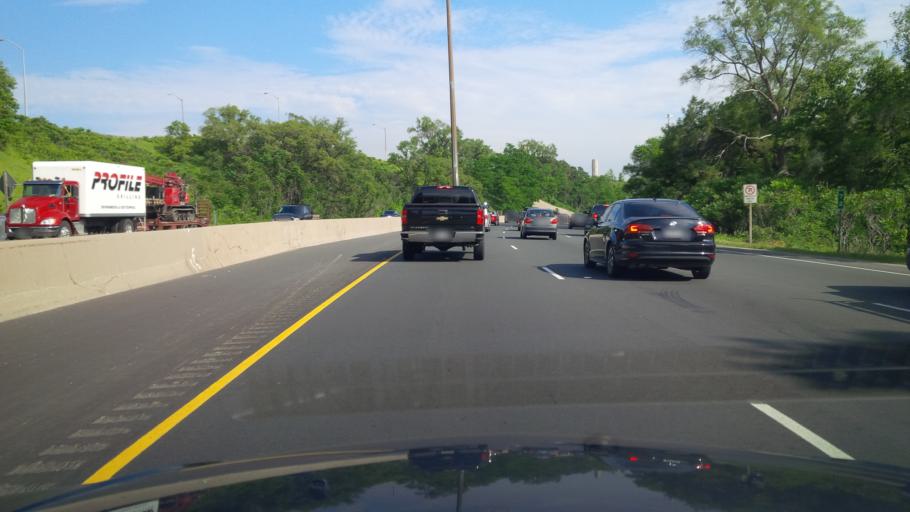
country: CA
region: Ontario
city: Hamilton
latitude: 43.2826
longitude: -79.8935
